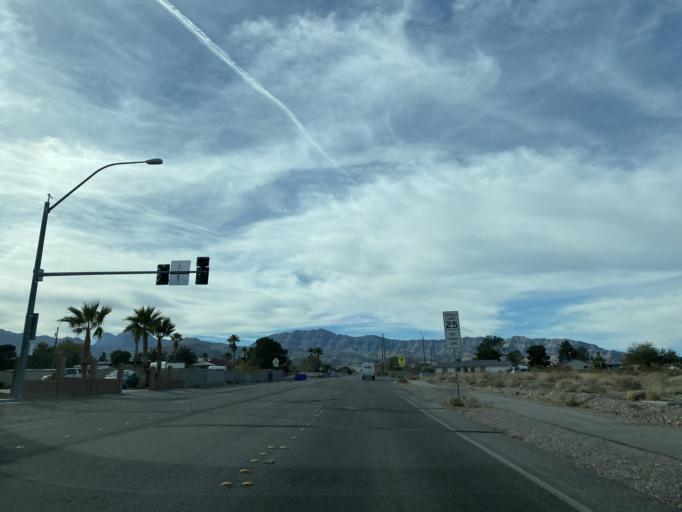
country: US
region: Nevada
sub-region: Clark County
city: Summerlin South
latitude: 36.2700
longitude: -115.3044
